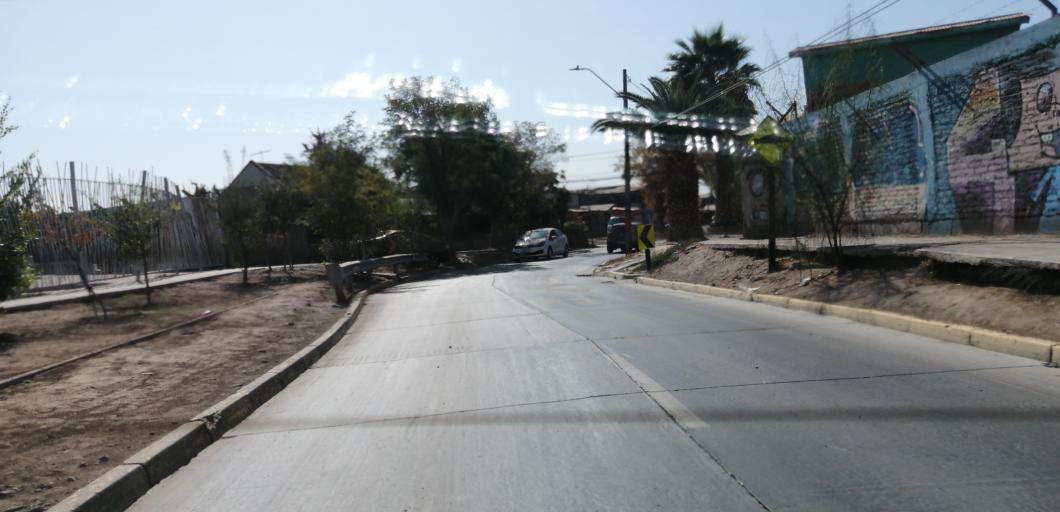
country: CL
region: Santiago Metropolitan
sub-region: Provincia de Santiago
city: Lo Prado
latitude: -33.4420
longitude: -70.7465
